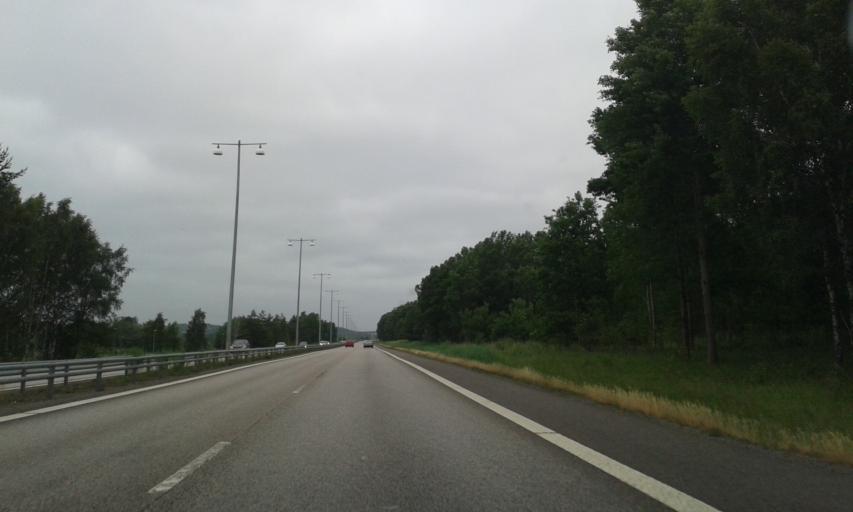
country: SE
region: Vaestra Goetaland
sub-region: Goteborg
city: Hammarkullen
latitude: 57.7723
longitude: 12.0088
